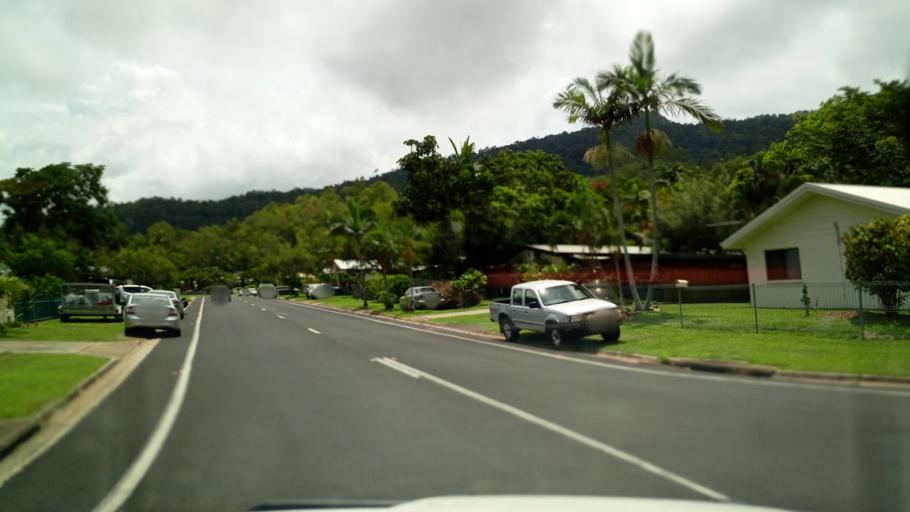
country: AU
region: Queensland
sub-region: Cairns
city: Yorkeys Knob
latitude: -16.8348
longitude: 145.6867
